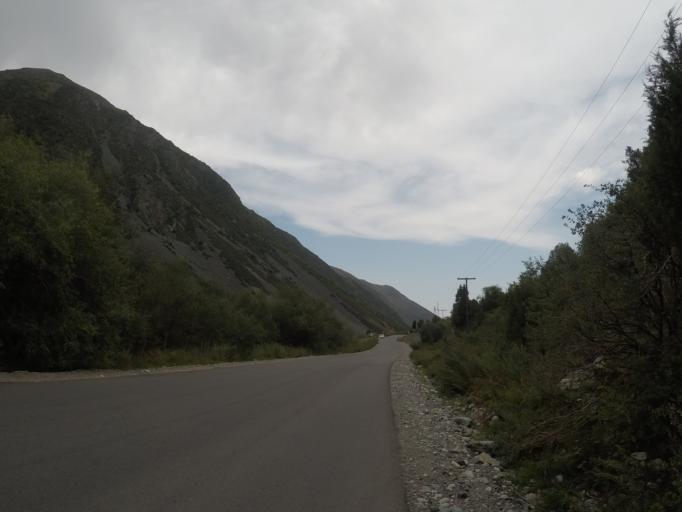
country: KG
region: Chuy
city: Bishkek
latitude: 42.5772
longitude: 74.4817
